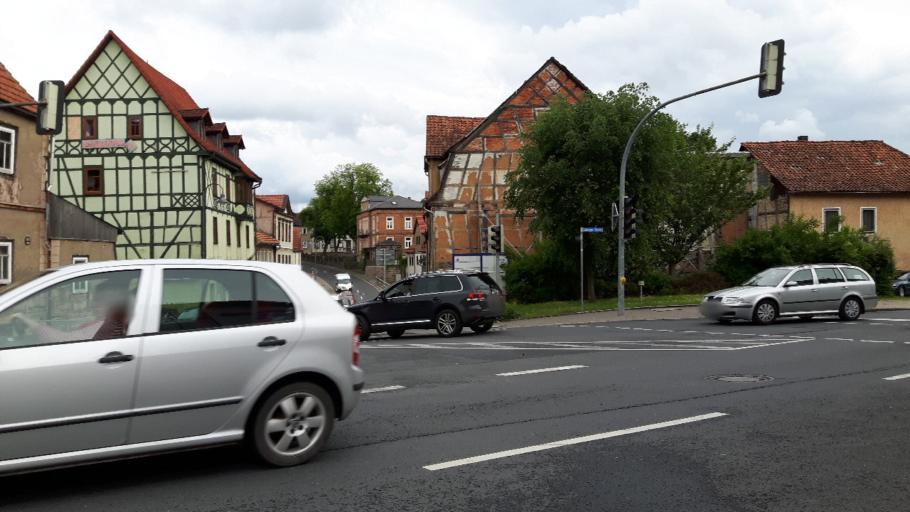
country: DE
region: Thuringia
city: Hildburghausen
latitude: 50.4253
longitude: 10.7326
